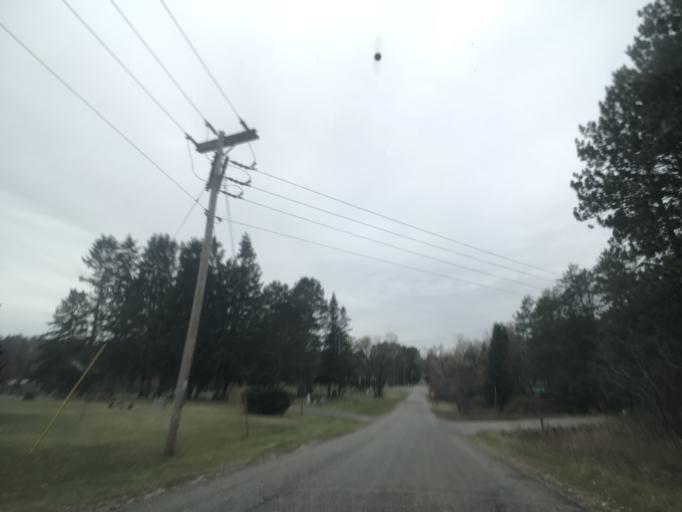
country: US
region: Wisconsin
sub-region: Menominee County
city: Legend Lake
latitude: 45.1811
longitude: -88.4655
